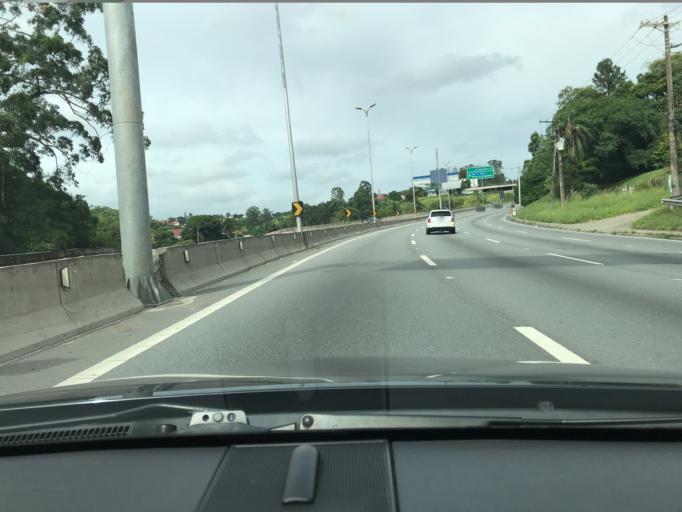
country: BR
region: Sao Paulo
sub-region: Taboao Da Serra
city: Taboao da Serra
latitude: -23.5913
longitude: -46.8194
